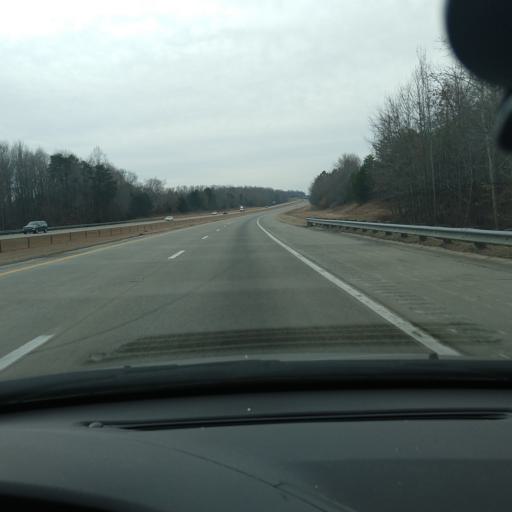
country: US
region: North Carolina
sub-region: Davidson County
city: Midway
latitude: 35.9291
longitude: -80.2316
